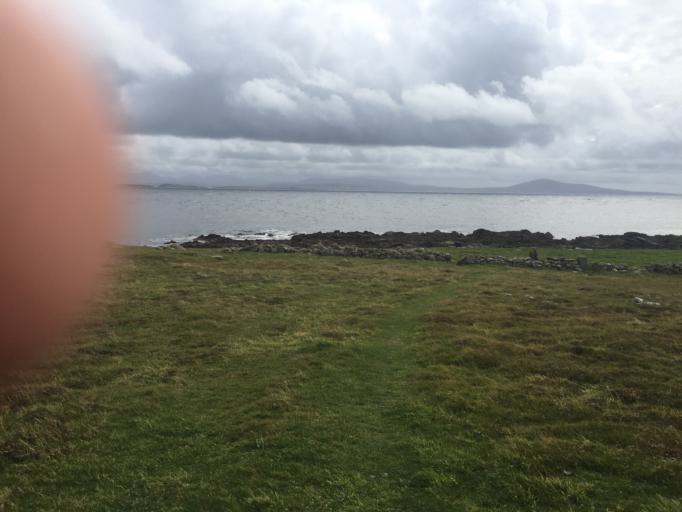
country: IE
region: Ulster
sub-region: County Donegal
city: Derrybeg
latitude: 55.2549
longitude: -8.1953
